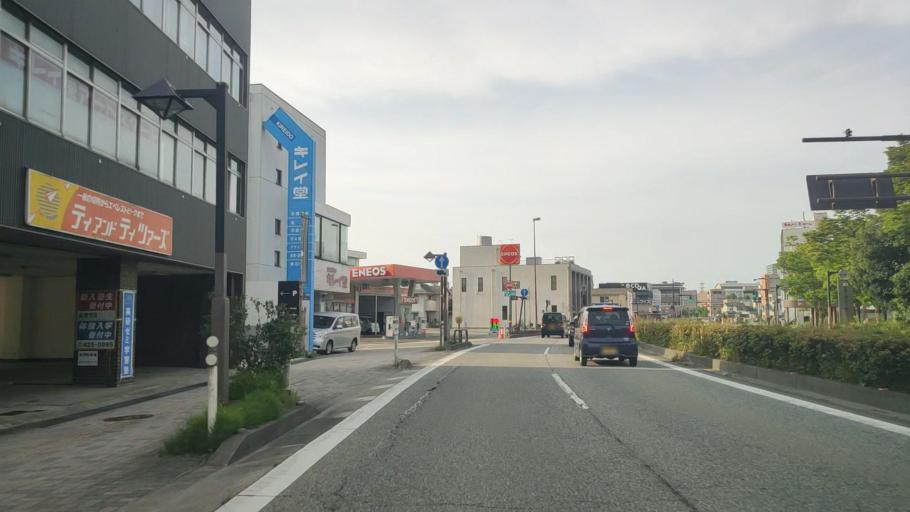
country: JP
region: Toyama
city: Toyama-shi
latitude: 36.6802
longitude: 137.2109
